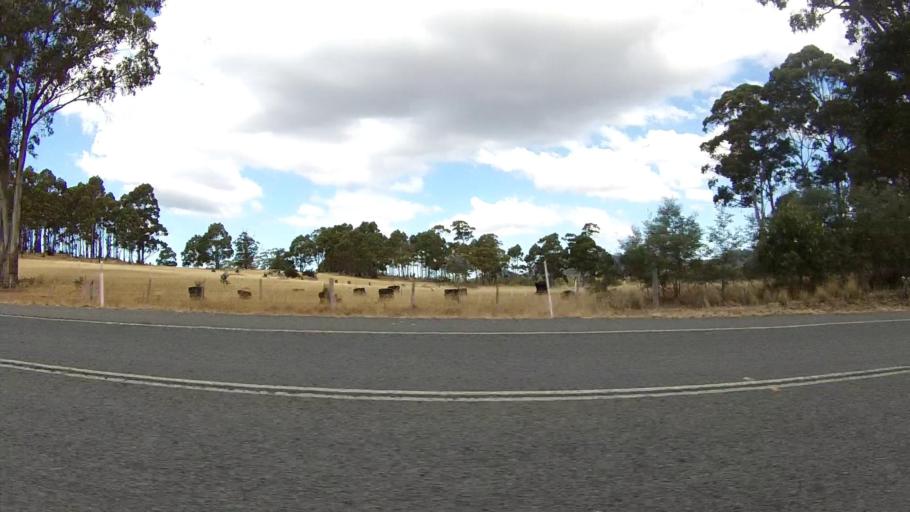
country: AU
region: Tasmania
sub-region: Sorell
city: Sorell
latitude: -42.6345
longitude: 147.6231
